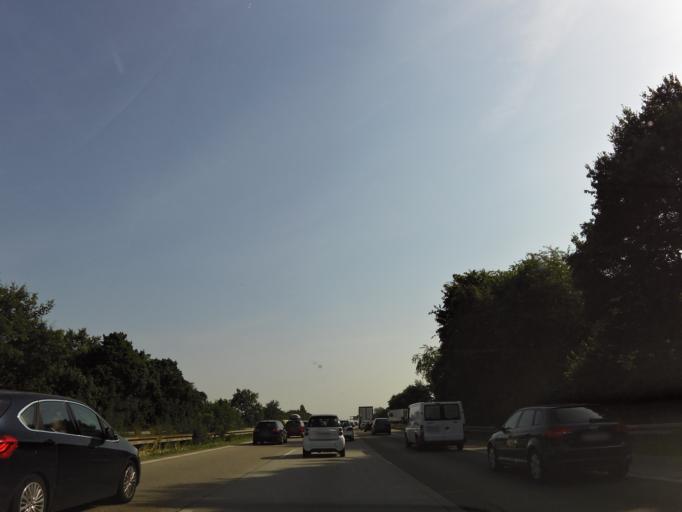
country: DE
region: Baden-Wuerttemberg
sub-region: Karlsruhe Region
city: Sankt Leon-Rot
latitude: 49.2577
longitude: 8.6030
